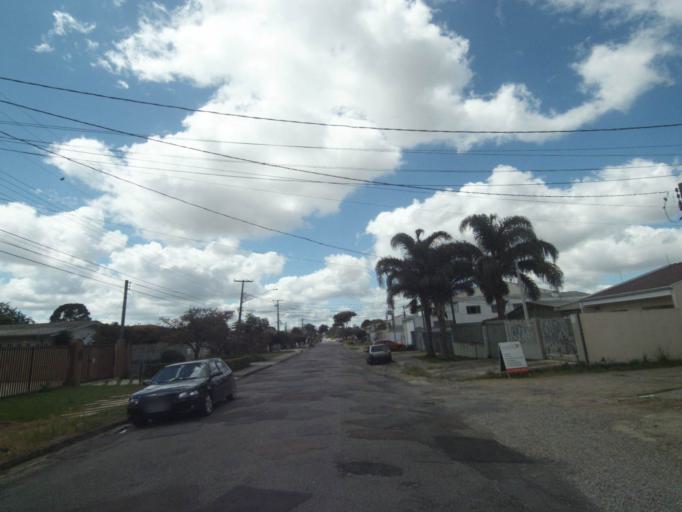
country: BR
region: Parana
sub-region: Pinhais
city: Pinhais
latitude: -25.4394
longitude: -49.2118
